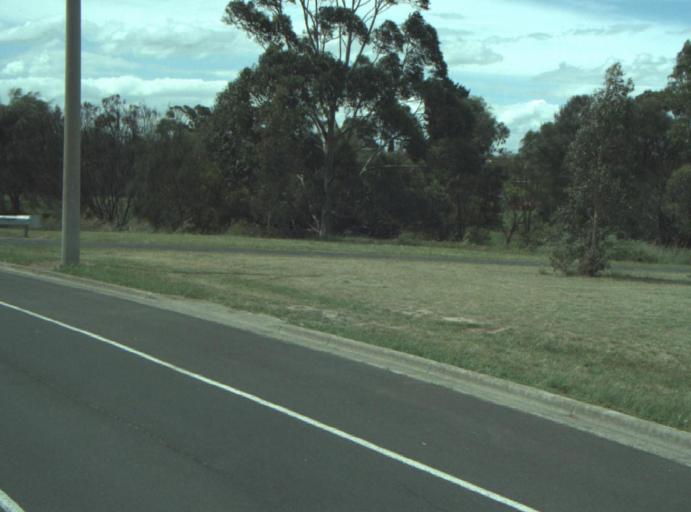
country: AU
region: Victoria
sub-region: Greater Geelong
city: Bell Park
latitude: -38.0931
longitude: 144.3414
